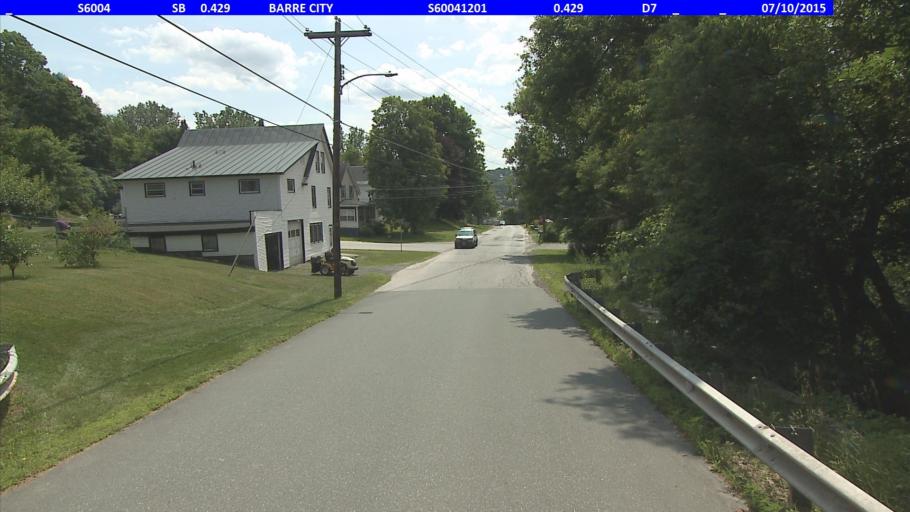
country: US
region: Vermont
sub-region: Washington County
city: Barre
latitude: 44.2116
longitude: -72.5109
